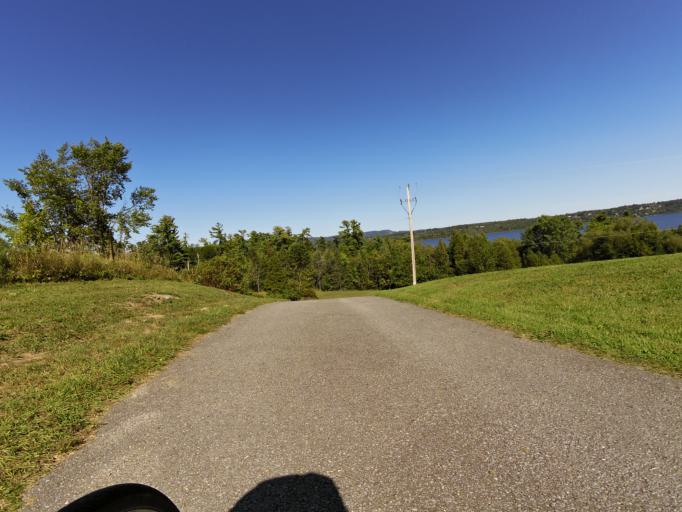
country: CA
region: Ontario
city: Bells Corners
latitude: 45.4420
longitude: -75.9551
